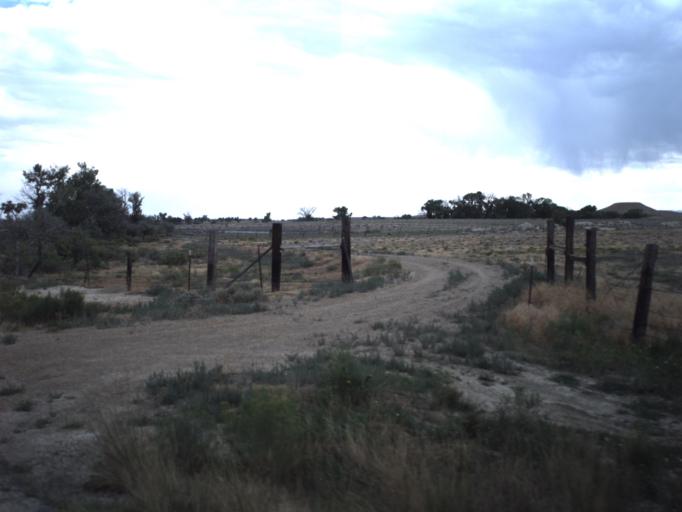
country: US
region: Utah
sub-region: Emery County
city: Huntington
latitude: 39.4089
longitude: -110.8532
